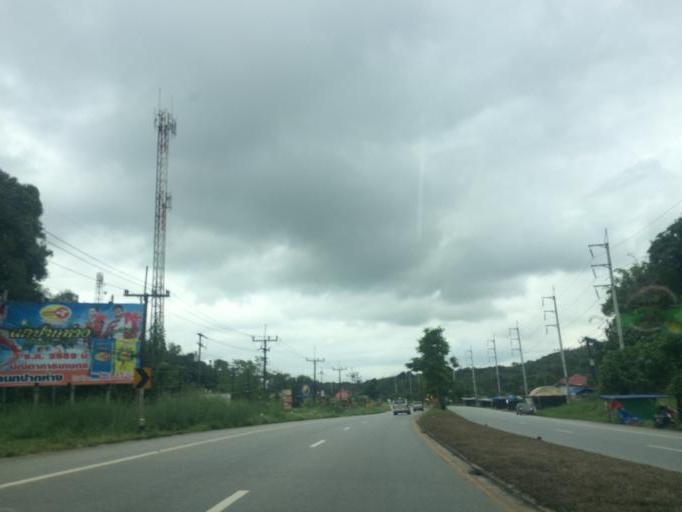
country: TH
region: Chiang Rai
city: Mae Chan
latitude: 20.1225
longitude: 99.8681
